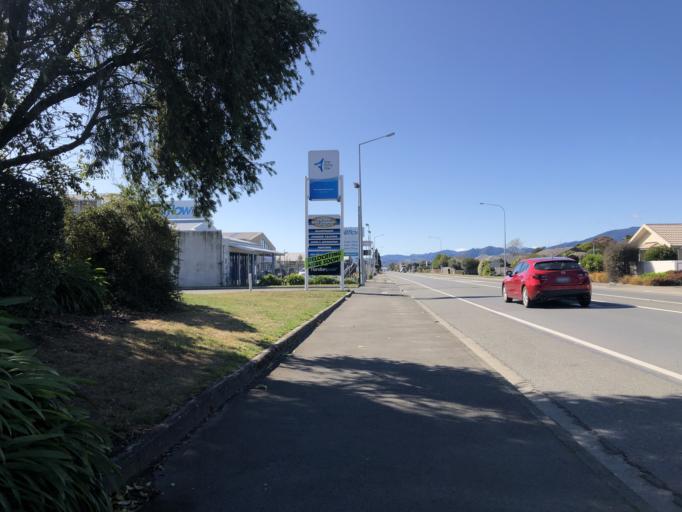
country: NZ
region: Tasman
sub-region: Tasman District
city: Richmond
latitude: -41.3434
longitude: 173.1707
